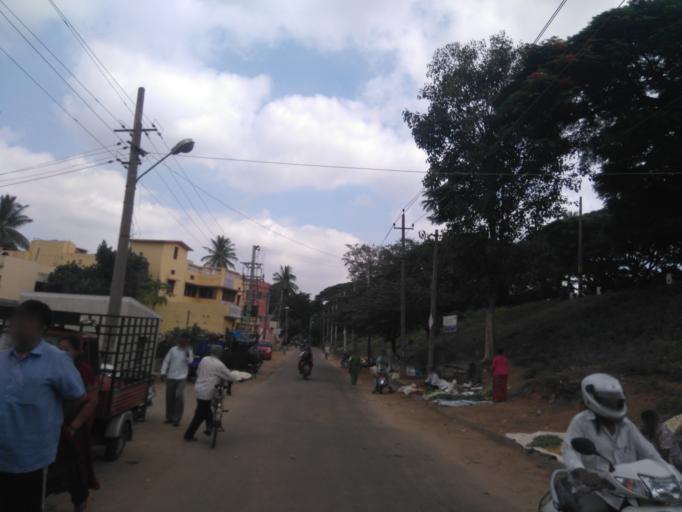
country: IN
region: Karnataka
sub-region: Mysore
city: Mysore
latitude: 12.2984
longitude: 76.6575
